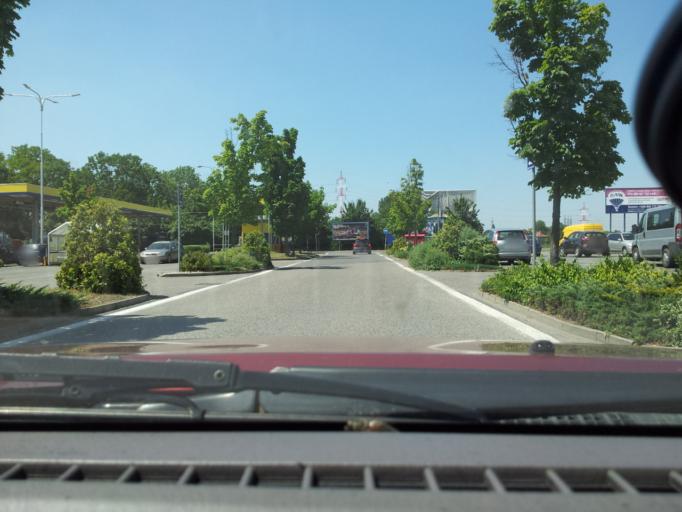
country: CZ
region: South Moravian
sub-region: Mesto Brno
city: Brno
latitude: 49.1616
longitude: 16.6382
